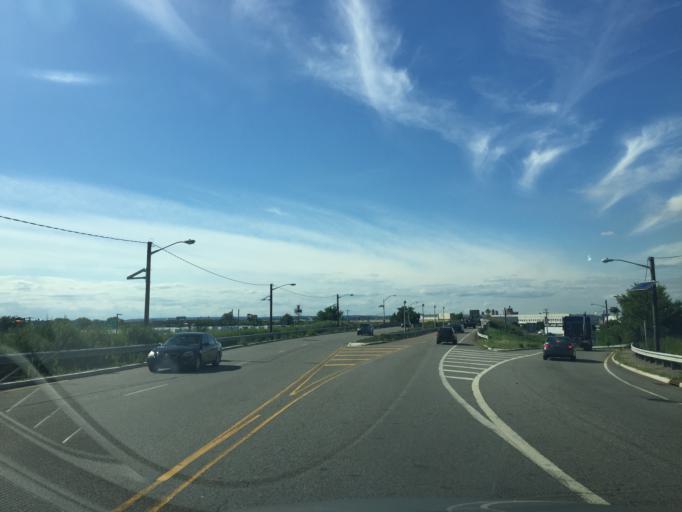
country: US
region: New Jersey
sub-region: Union County
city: Elizabeth
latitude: 40.6685
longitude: -74.1804
